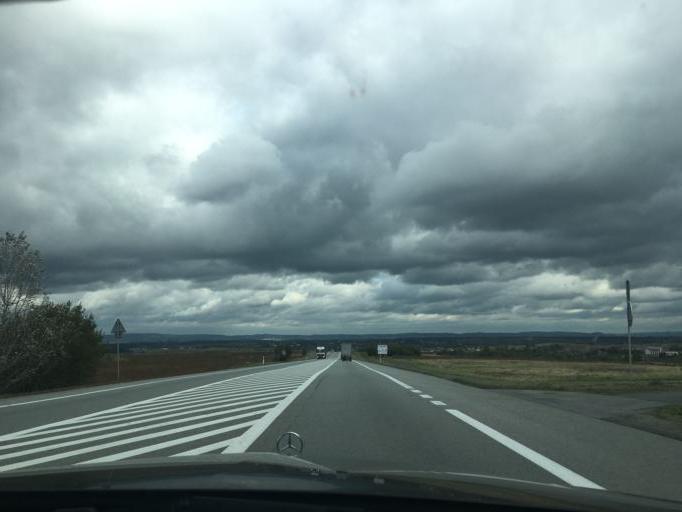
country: PL
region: Subcarpathian Voivodeship
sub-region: Powiat krosnienski
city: Miejsce Piastowe
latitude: 49.6077
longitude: 21.7382
